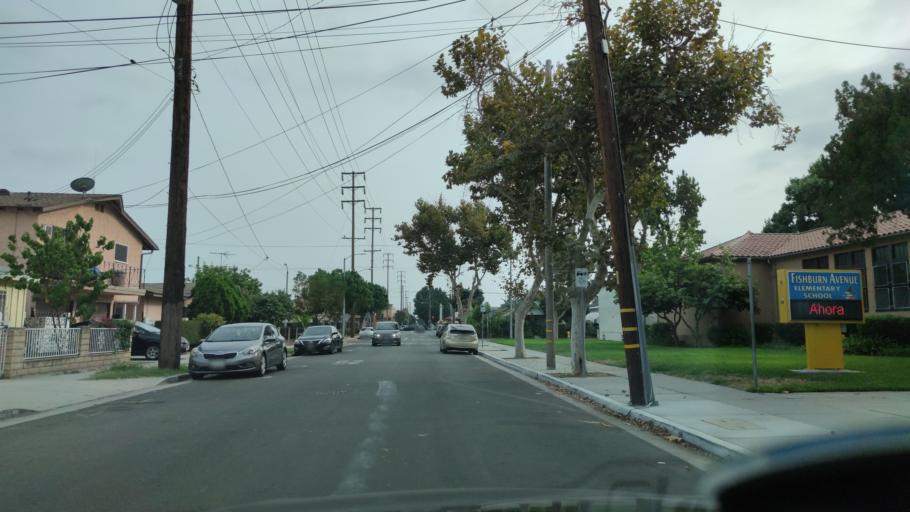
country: US
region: California
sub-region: Los Angeles County
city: Maywood
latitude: 33.9892
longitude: -118.1898
